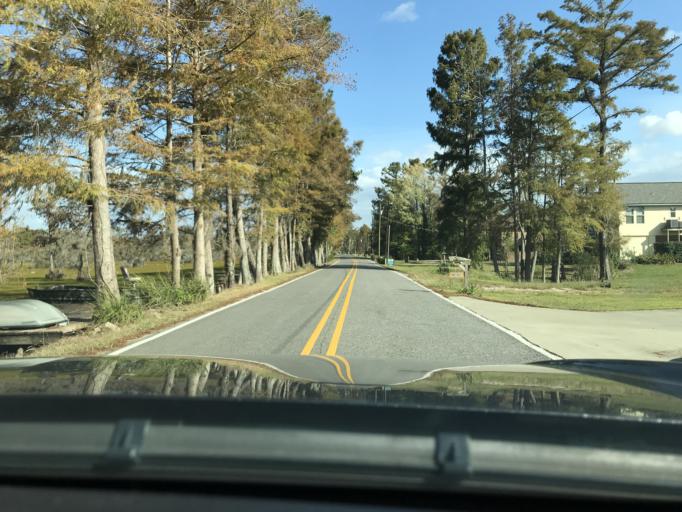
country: US
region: Louisiana
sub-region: Calcasieu Parish
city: Westlake
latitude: 30.3168
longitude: -93.2925
